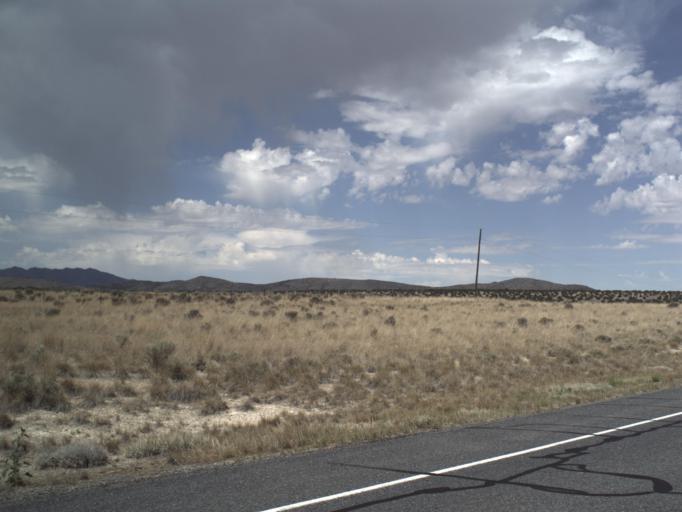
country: US
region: Utah
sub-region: Utah County
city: Eagle Mountain
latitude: 40.0584
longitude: -112.3082
